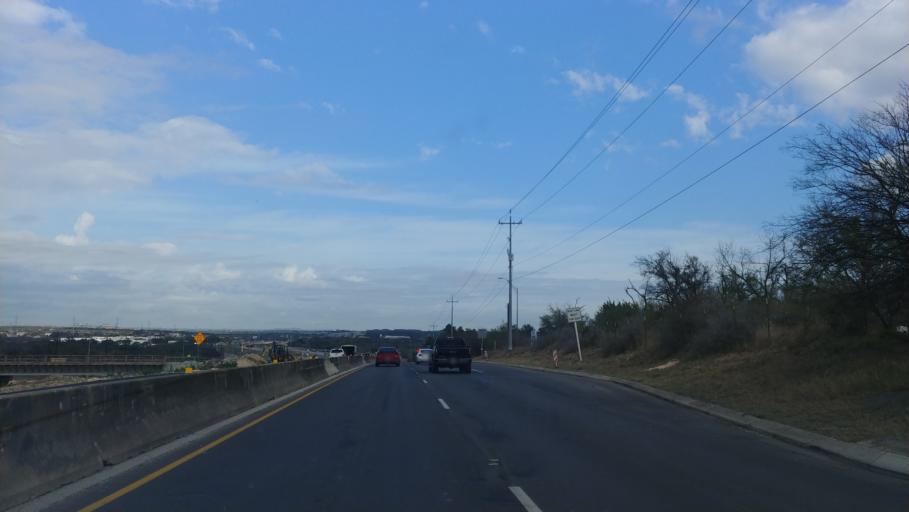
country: US
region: Texas
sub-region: Bexar County
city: Lackland Air Force Base
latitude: 29.4157
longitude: -98.7091
